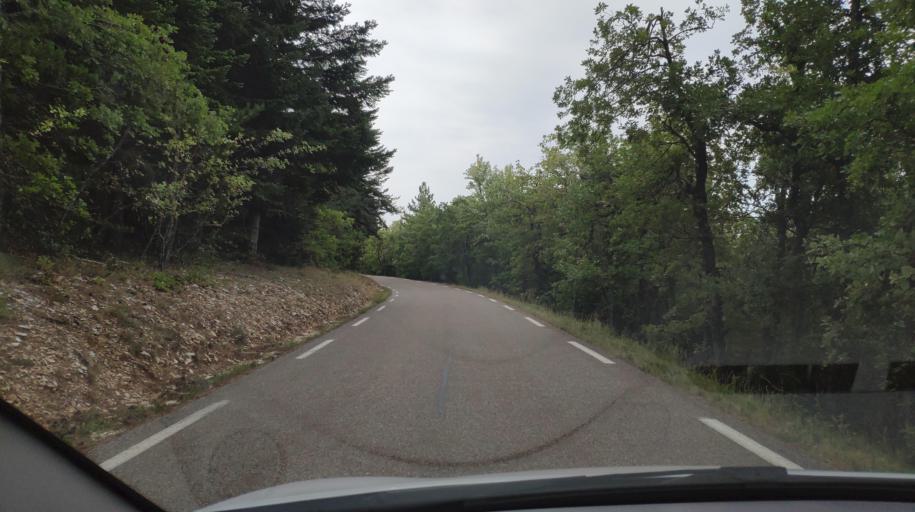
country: FR
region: Provence-Alpes-Cote d'Azur
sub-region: Departement du Vaucluse
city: Sault
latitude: 44.1447
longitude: 5.3665
